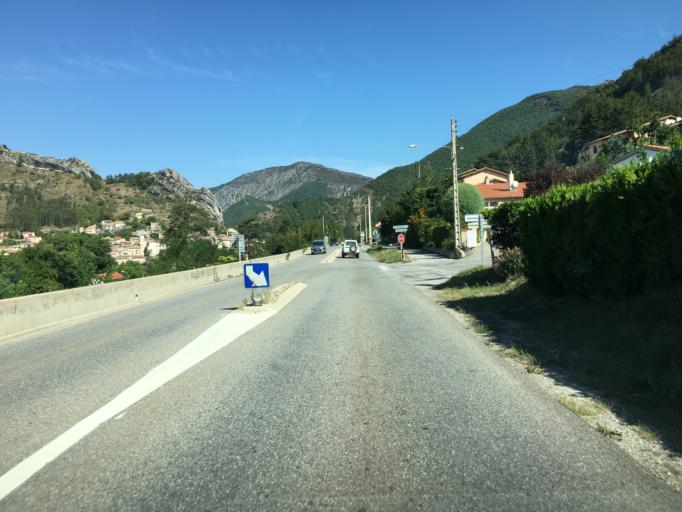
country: FR
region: Provence-Alpes-Cote d'Azur
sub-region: Departement des Hautes-Alpes
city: Serres
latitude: 44.4235
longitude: 5.7192
